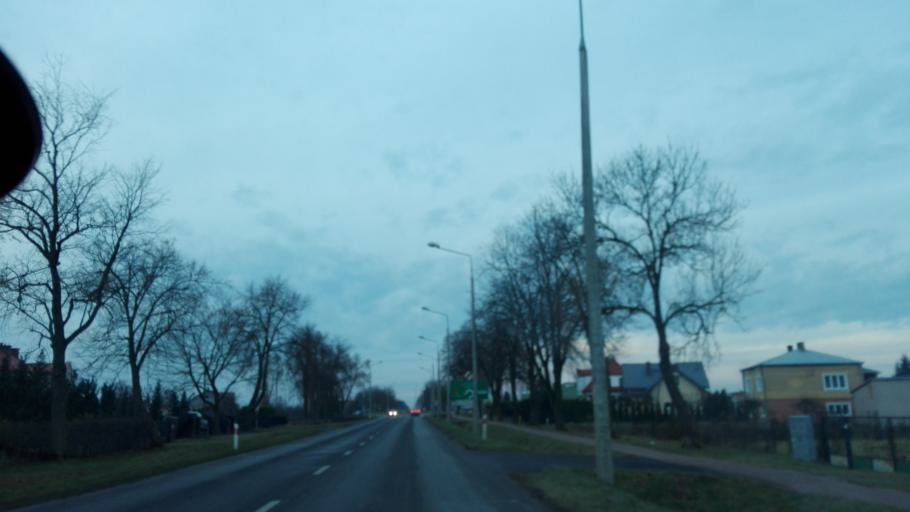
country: PL
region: Lublin Voivodeship
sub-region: Powiat radzynski
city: Radzyn Podlaski
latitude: 51.7741
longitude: 22.6242
